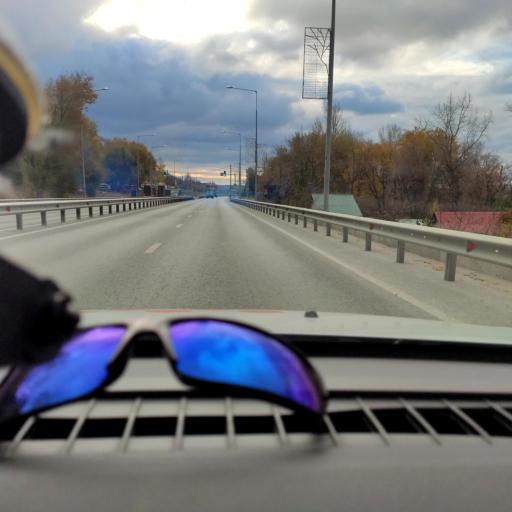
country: RU
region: Samara
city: Volzhskiy
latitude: 53.4041
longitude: 50.1462
